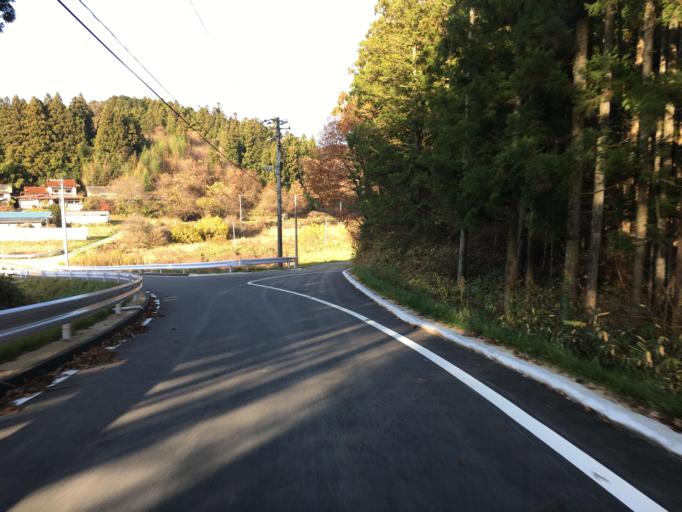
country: JP
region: Fukushima
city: Ishikawa
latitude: 37.2572
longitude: 140.5696
